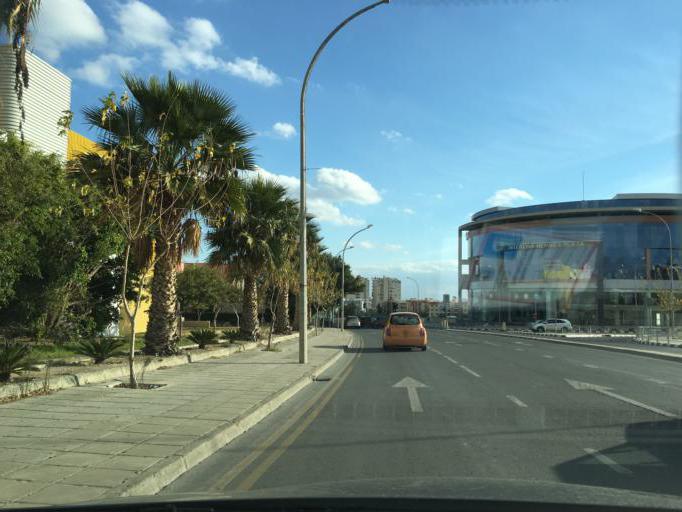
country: CY
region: Limassol
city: Limassol
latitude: 34.7009
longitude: 33.0604
